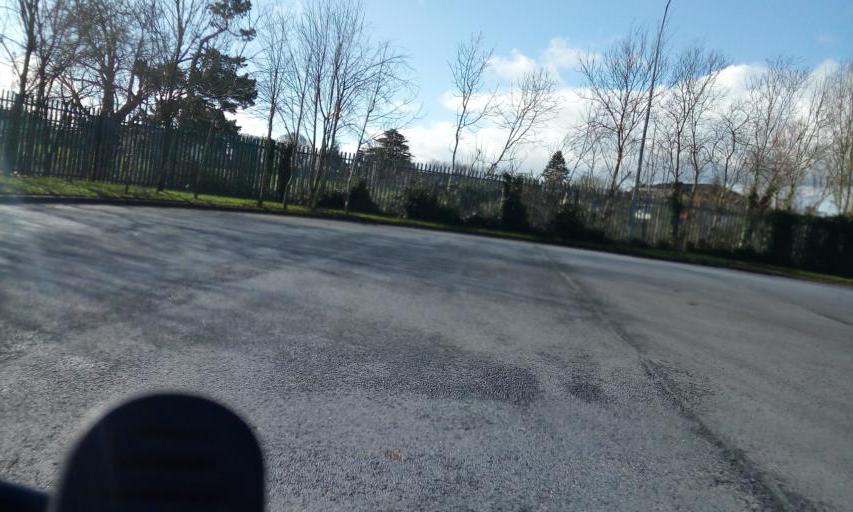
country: IE
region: Leinster
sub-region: Kilkenny
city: Kilkenny
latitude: 52.6526
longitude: -7.2339
